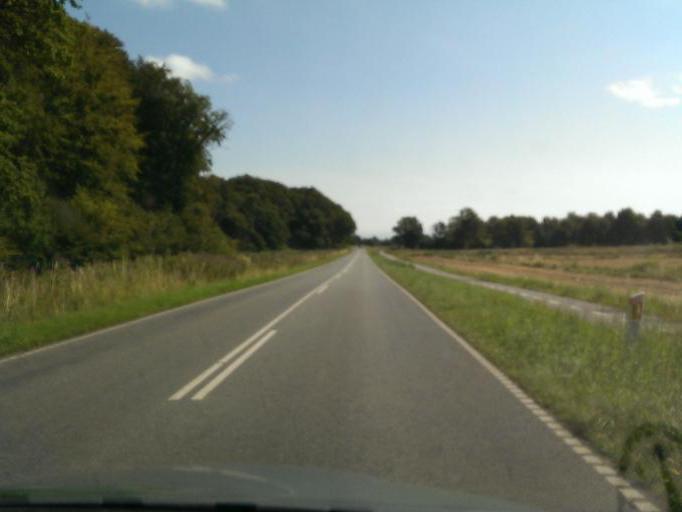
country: DK
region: Central Jutland
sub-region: Syddjurs Kommune
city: Ebeltoft
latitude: 56.2352
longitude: 10.5854
